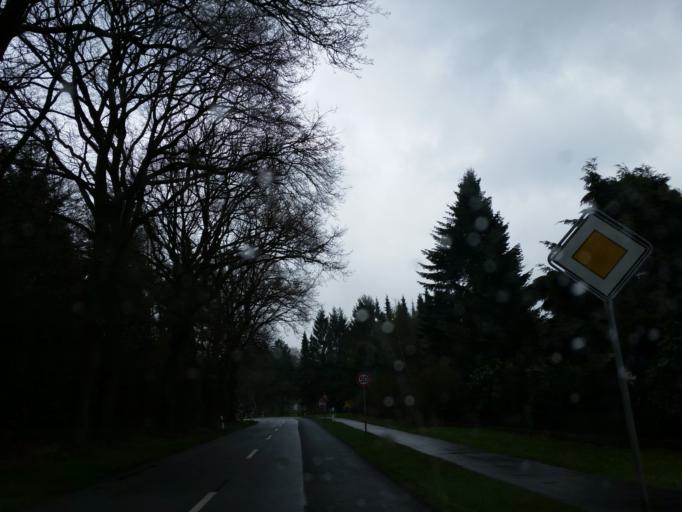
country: DE
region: Lower Saxony
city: Oerel
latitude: 53.4948
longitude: 9.0302
